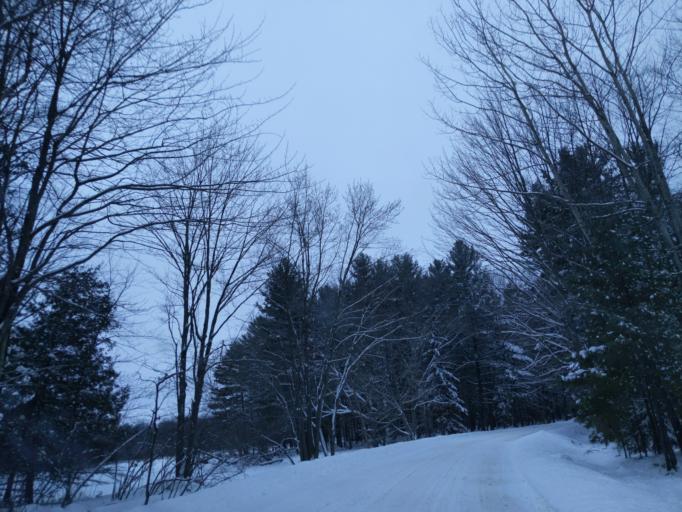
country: US
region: Wisconsin
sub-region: Marathon County
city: Mosinee
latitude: 44.7613
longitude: -89.8682
